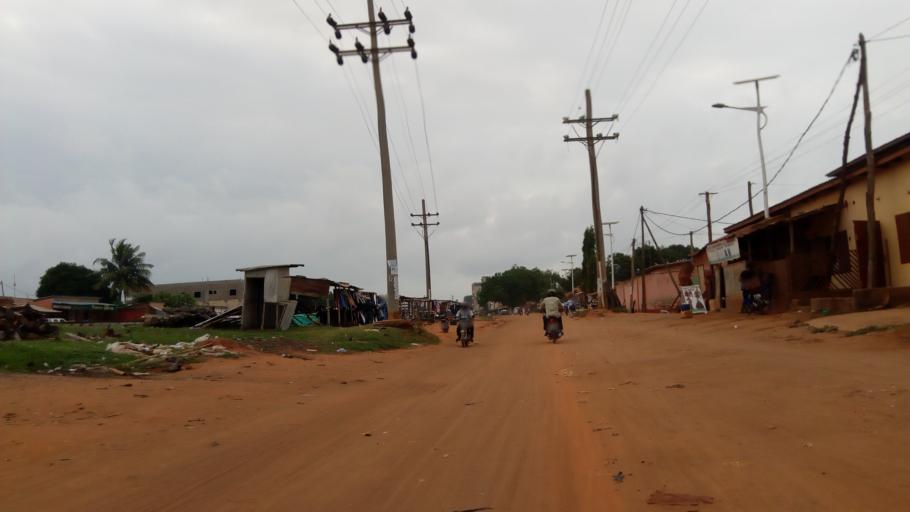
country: TG
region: Maritime
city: Lome
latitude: 6.1629
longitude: 1.2064
